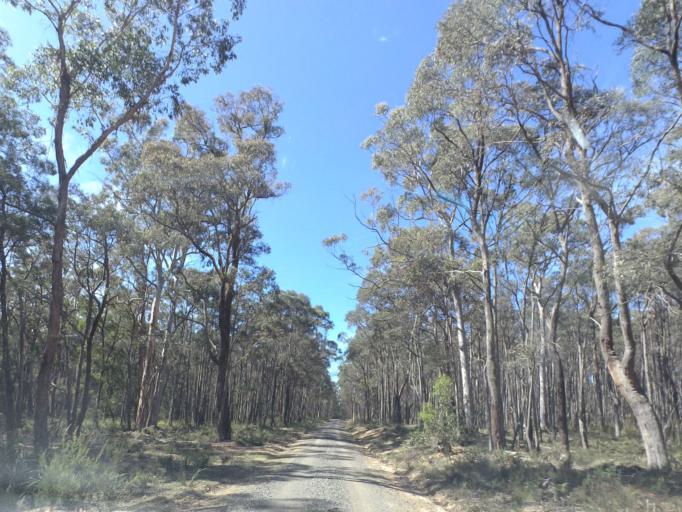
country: AU
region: Victoria
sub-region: Moorabool
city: Bacchus Marsh
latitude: -37.4122
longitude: 144.3304
